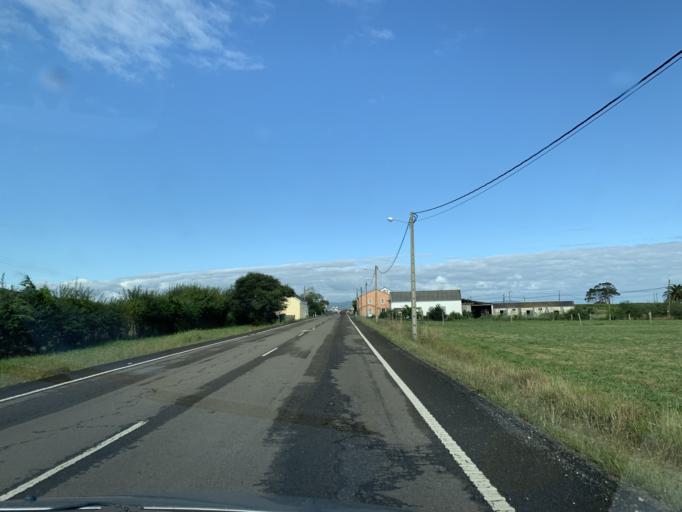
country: ES
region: Galicia
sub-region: Provincia de Lugo
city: Ribadeo
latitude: 43.5485
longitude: -7.1300
